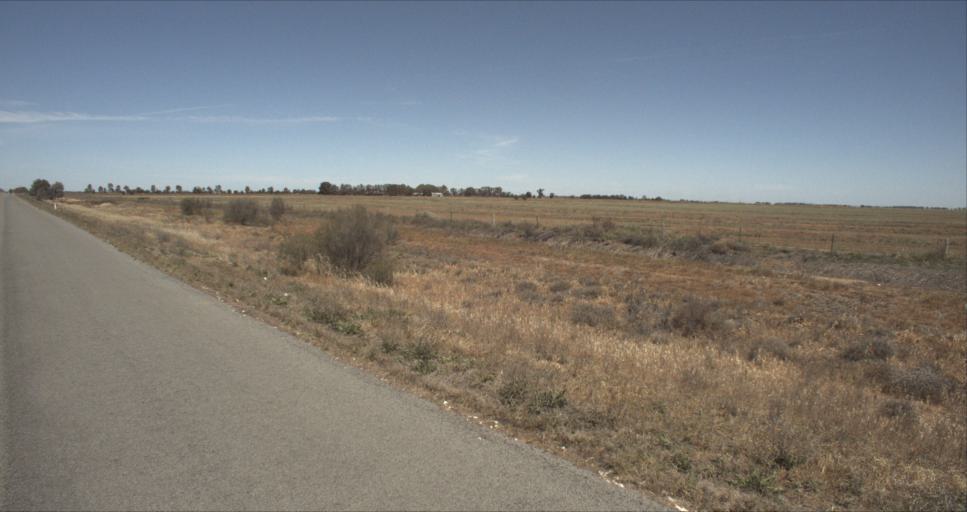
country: AU
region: New South Wales
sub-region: Leeton
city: Leeton
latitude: -34.4341
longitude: 146.2991
